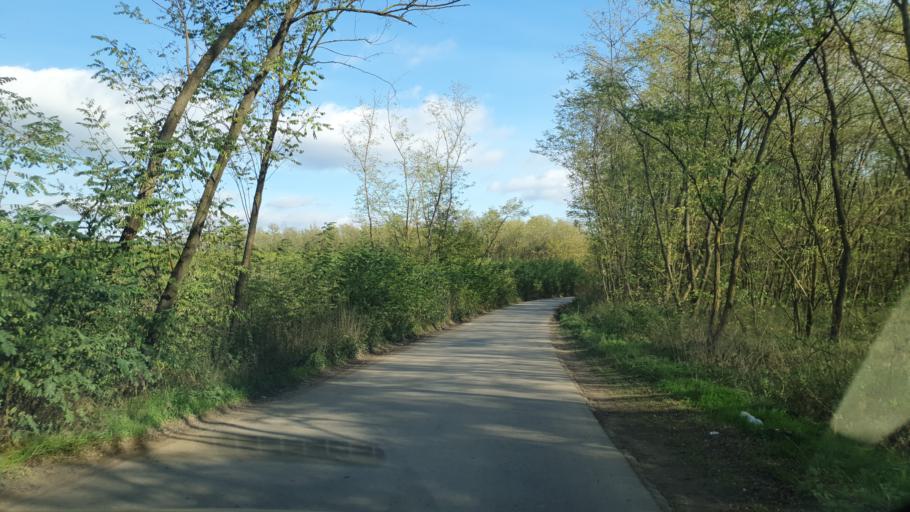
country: HU
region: Szabolcs-Szatmar-Bereg
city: Nyirtass
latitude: 48.1208
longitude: 22.0665
